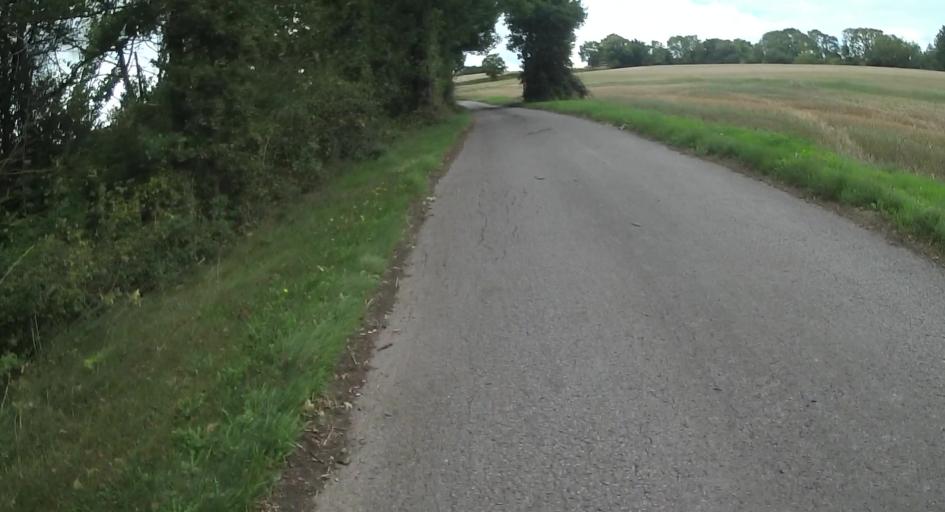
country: GB
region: England
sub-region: West Berkshire
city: Thatcham
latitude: 51.4008
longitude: -1.2278
